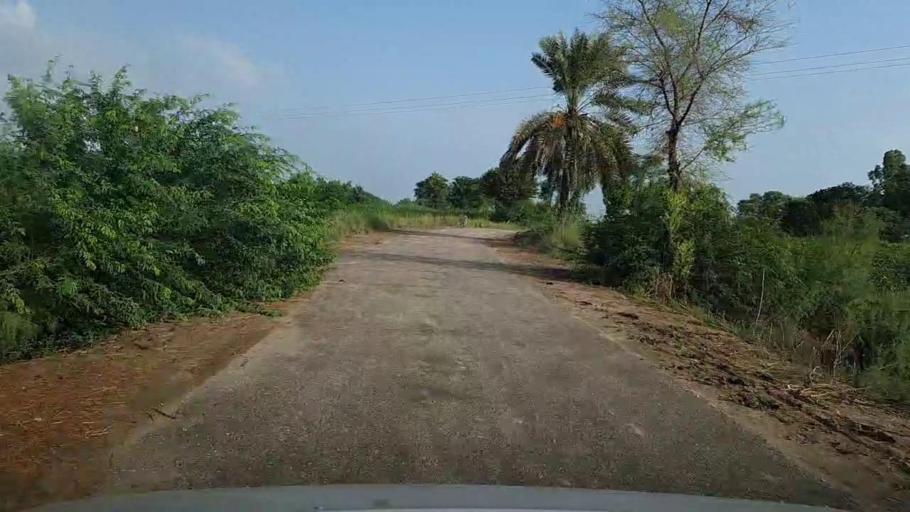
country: PK
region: Sindh
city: Pad Idan
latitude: 26.8014
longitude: 68.2360
